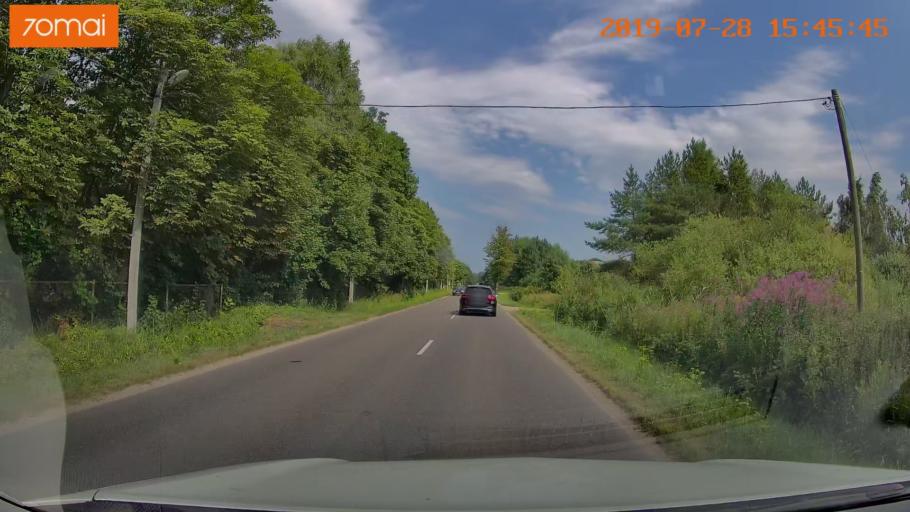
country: RU
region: Kaliningrad
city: Otradnoye
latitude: 54.9422
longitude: 20.0446
